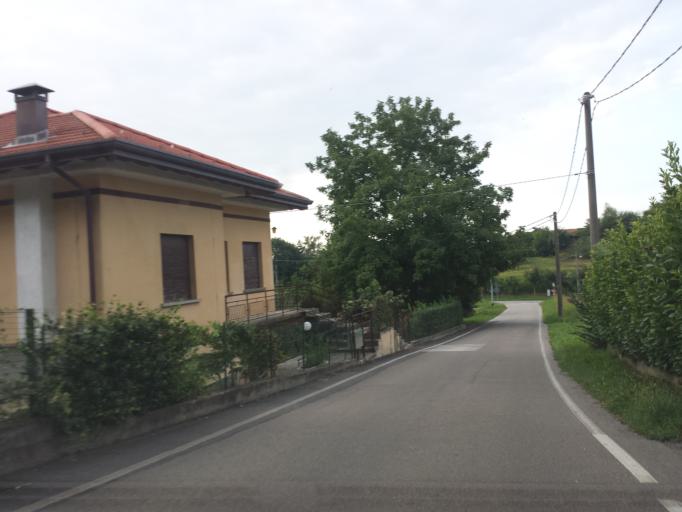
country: IT
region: Lombardy
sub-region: Provincia di Varese
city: Sesto Calende
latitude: 45.7347
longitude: 8.6182
